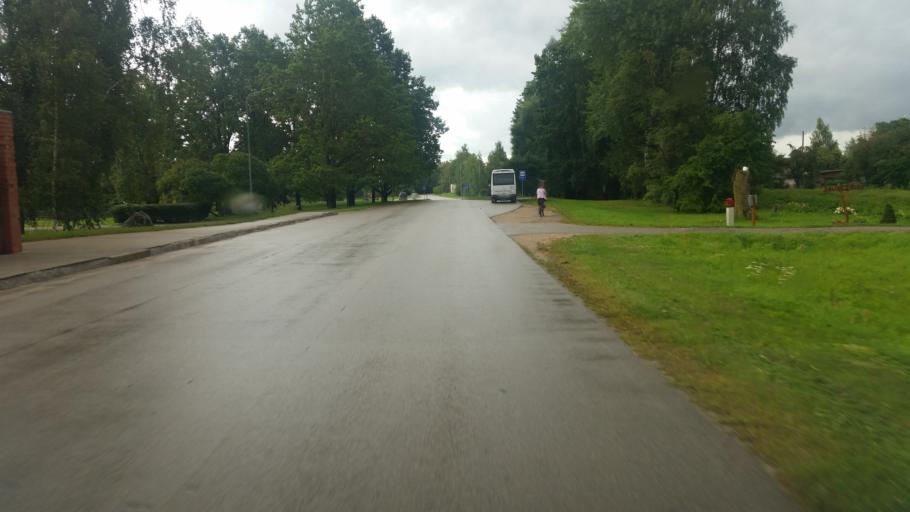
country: LV
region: Vecumnieki
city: Vecumnieki
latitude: 56.4324
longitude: 24.4624
